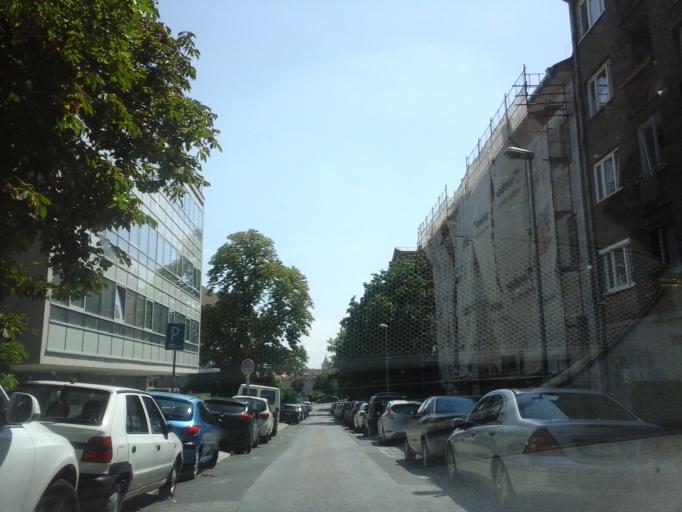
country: SK
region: Bratislavsky
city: Bratislava
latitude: 48.1453
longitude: 17.1013
